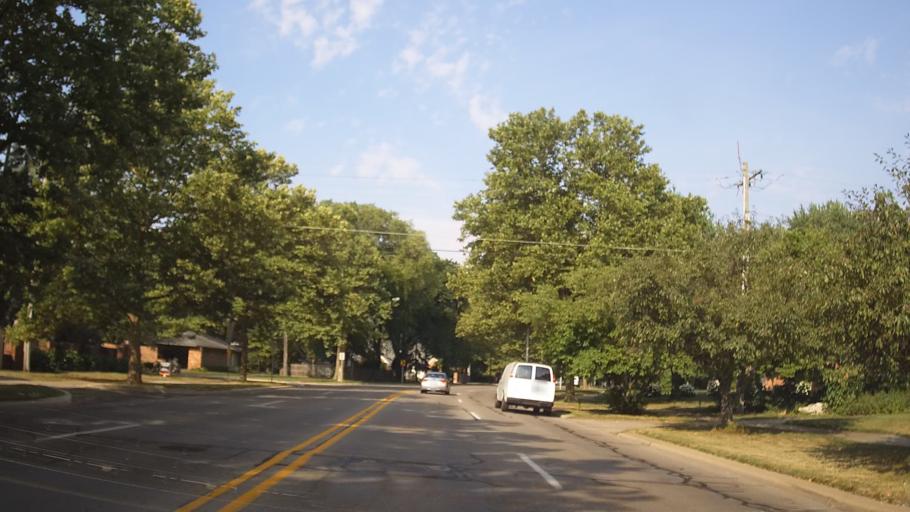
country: US
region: Michigan
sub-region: Wayne County
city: Grosse Pointe
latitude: 42.3811
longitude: -82.9148
